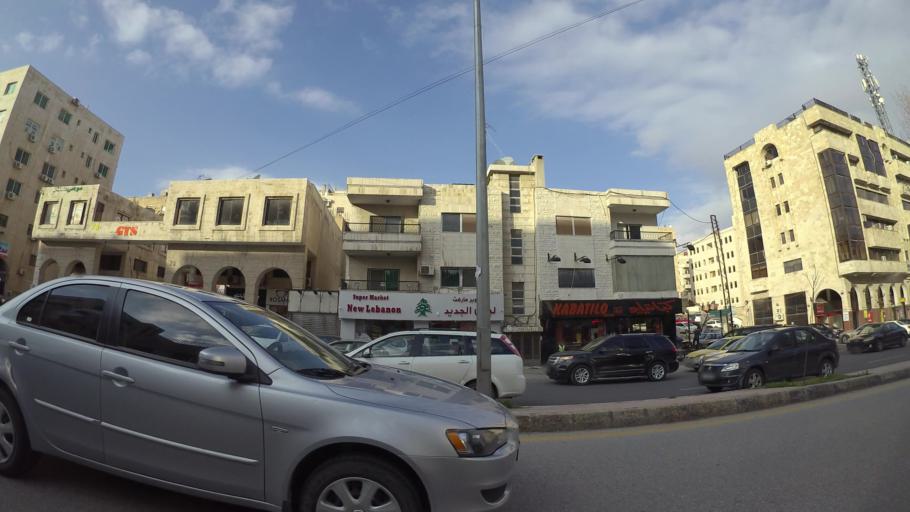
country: JO
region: Amman
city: Al Jubayhah
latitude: 31.9862
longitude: 35.8807
